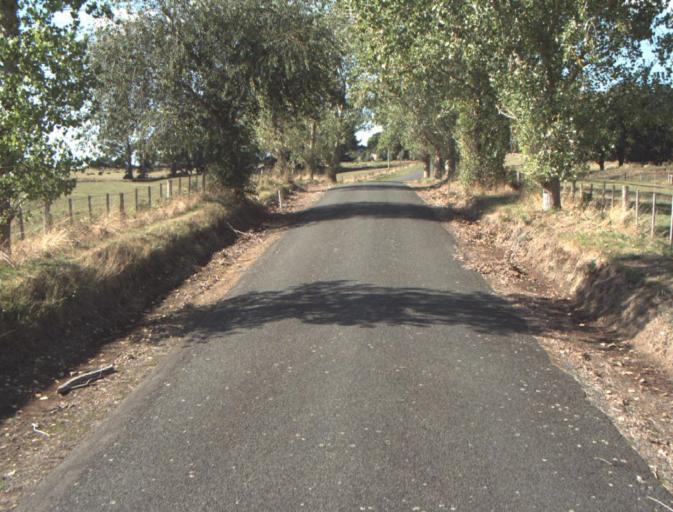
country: AU
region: Tasmania
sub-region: Launceston
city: Mayfield
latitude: -41.2876
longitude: 147.2115
